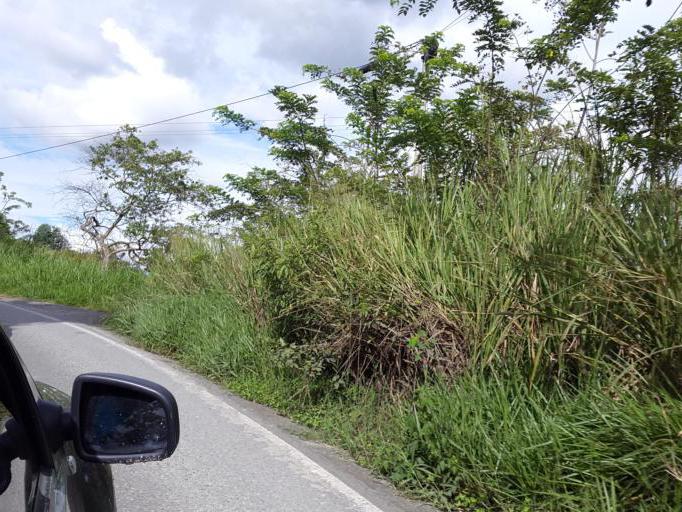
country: CO
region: Quindio
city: Cordoba
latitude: 4.4069
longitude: -75.7263
